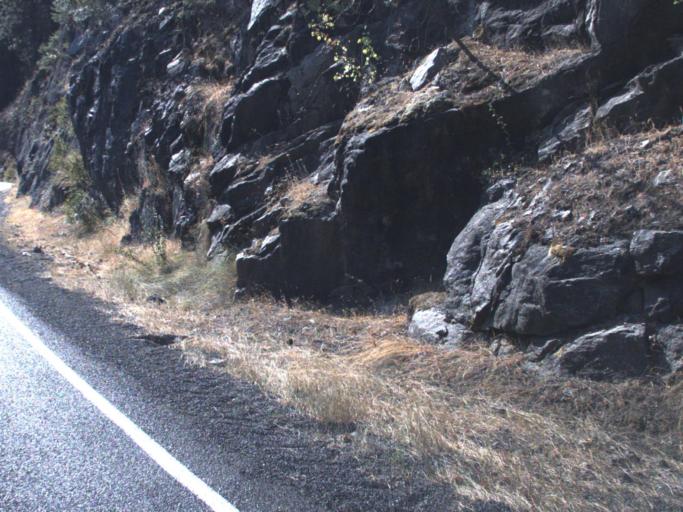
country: US
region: Washington
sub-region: Spokane County
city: Deer Park
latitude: 47.8768
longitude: -117.7032
